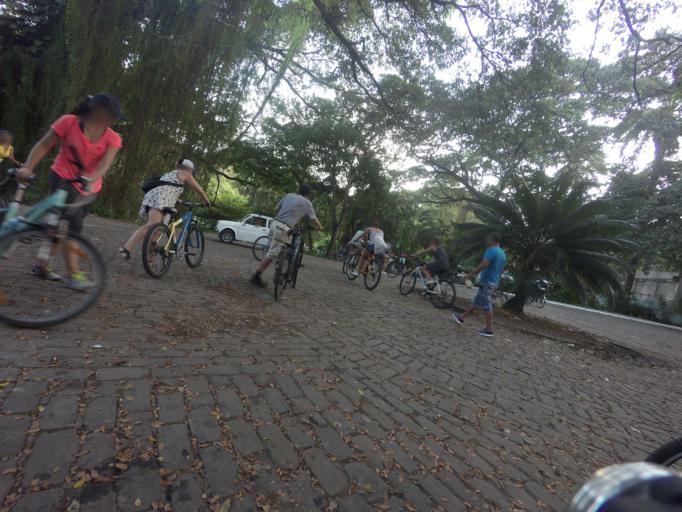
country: CU
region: La Habana
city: Cerro
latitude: 23.1088
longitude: -82.4071
